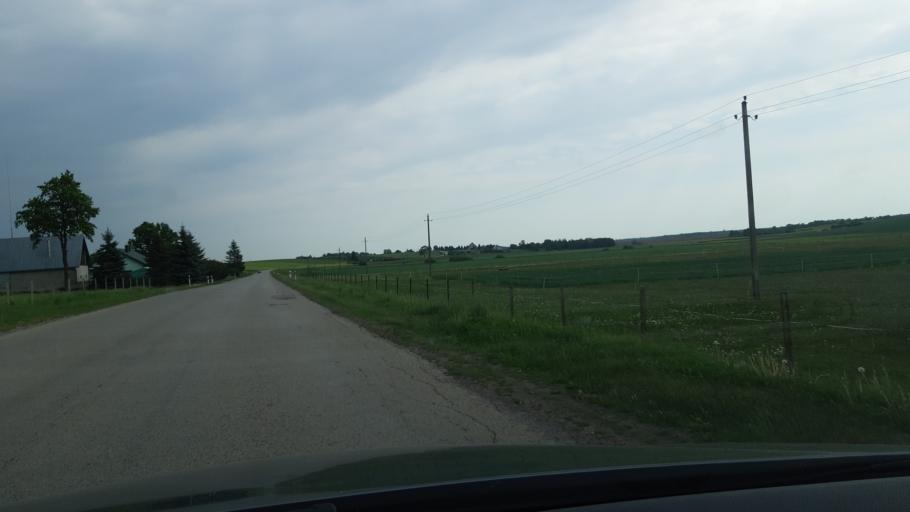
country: LT
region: Kauno apskritis
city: Kedainiai
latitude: 55.1705
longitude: 23.8532
